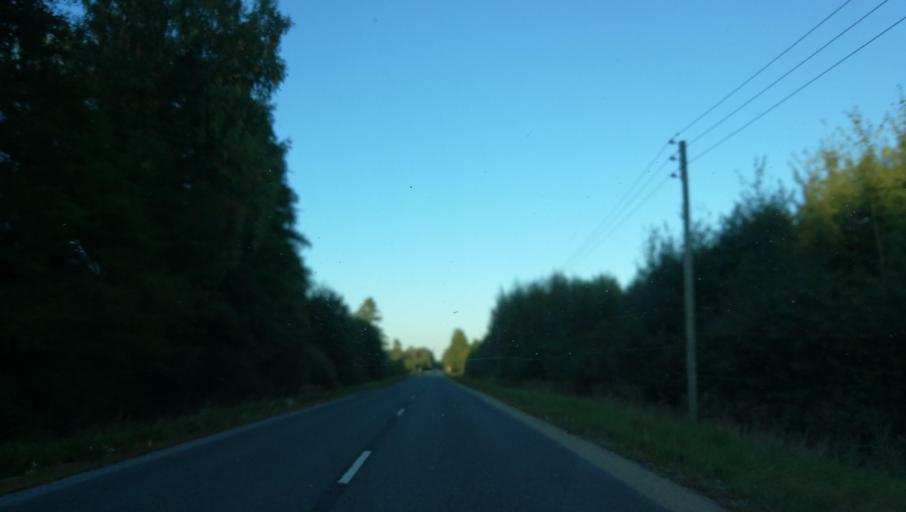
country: LV
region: Aizpute
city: Aizpute
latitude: 56.6238
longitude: 21.6990
